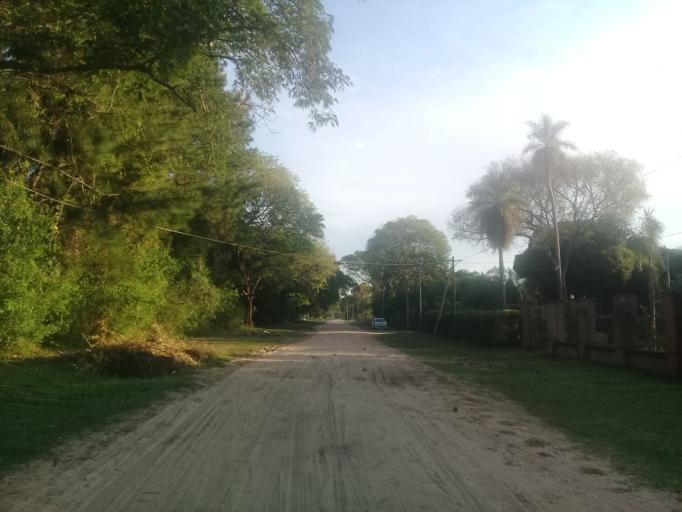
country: AR
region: Corrientes
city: San Luis del Palmar
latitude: -27.4505
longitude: -58.6557
